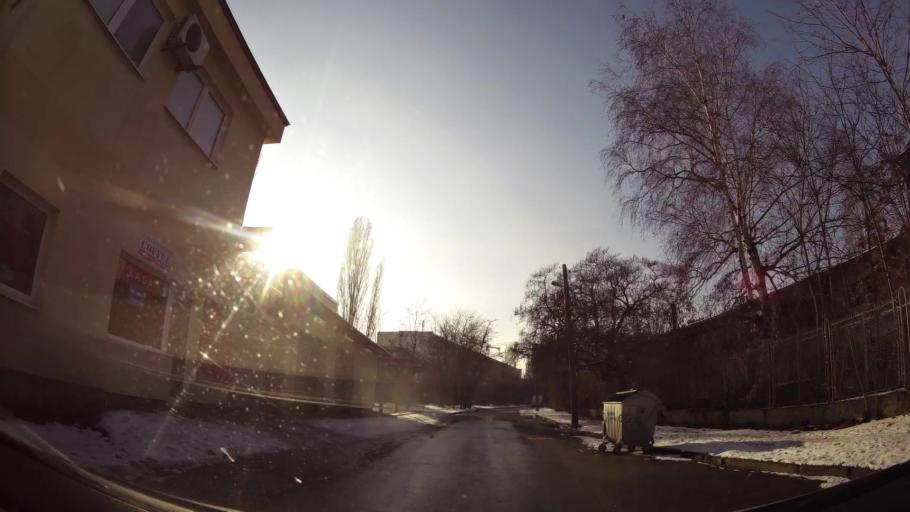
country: BG
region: Sofia-Capital
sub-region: Stolichna Obshtina
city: Sofia
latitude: 42.6681
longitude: 23.3512
